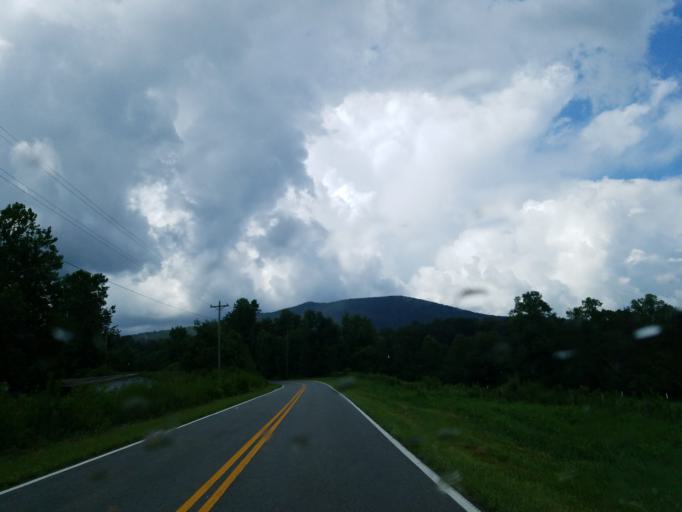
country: US
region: Georgia
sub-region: Gilmer County
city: Ellijay
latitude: 34.6716
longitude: -84.3837
